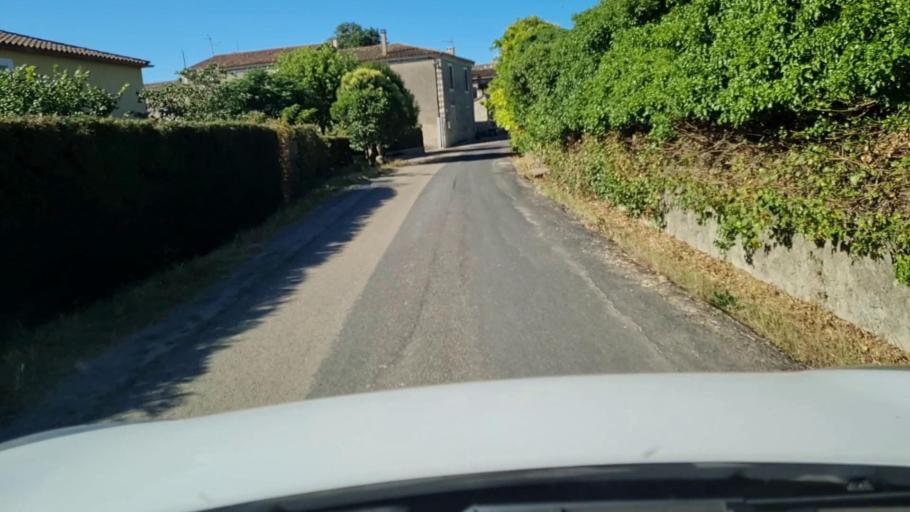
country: FR
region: Languedoc-Roussillon
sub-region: Departement du Gard
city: Sommieres
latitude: 43.8319
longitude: 4.0272
